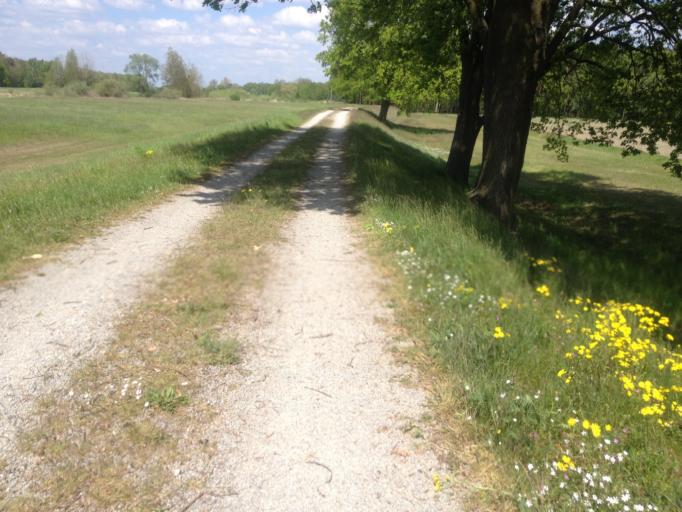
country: DE
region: Brandenburg
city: Drehnow
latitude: 51.8303
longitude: 14.3501
